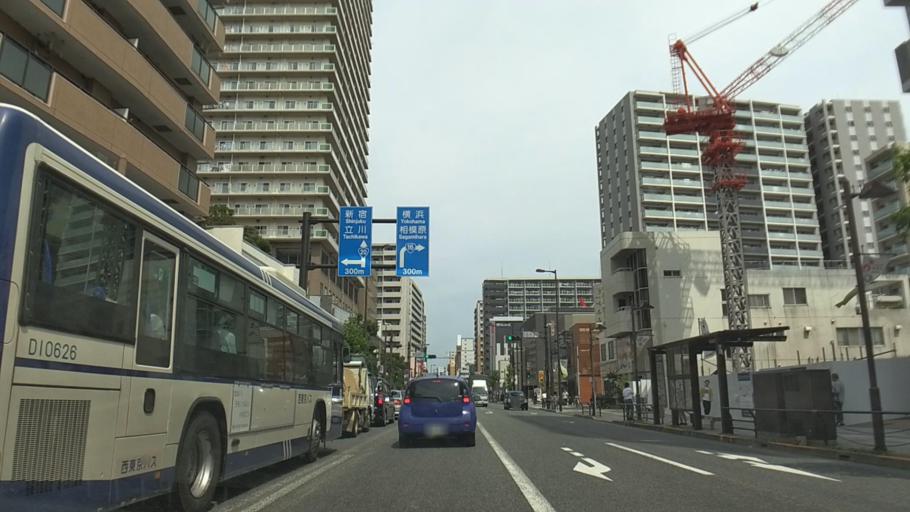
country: JP
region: Tokyo
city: Hachioji
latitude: 35.6603
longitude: 139.3294
